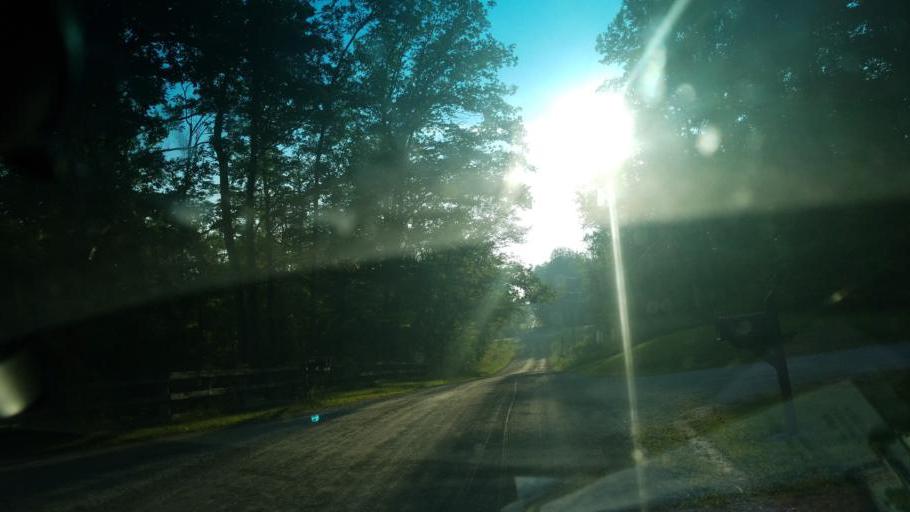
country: US
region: Ohio
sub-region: Richland County
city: Lexington
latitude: 40.5720
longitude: -82.6447
